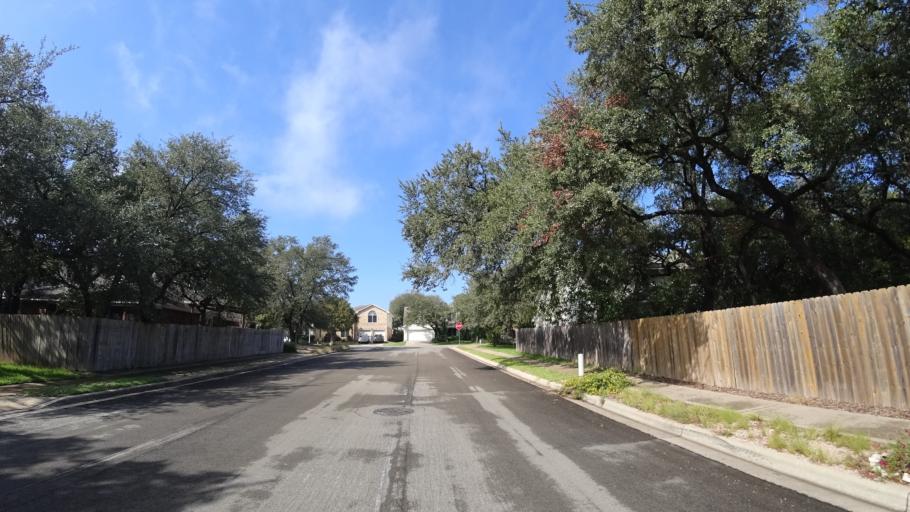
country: US
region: Texas
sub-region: Travis County
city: Shady Hollow
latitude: 30.2056
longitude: -97.8751
